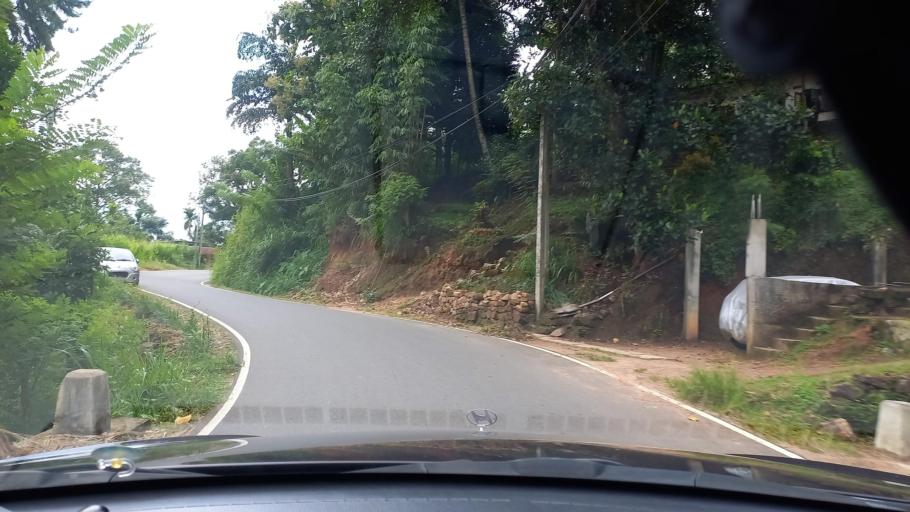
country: LK
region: Central
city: Gampola
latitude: 7.2271
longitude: 80.6054
